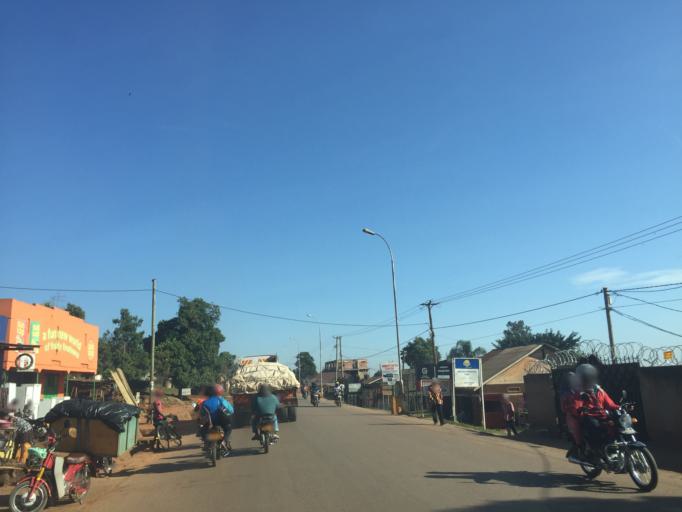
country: UG
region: Central Region
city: Kampala Central Division
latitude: 0.3676
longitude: 32.5693
